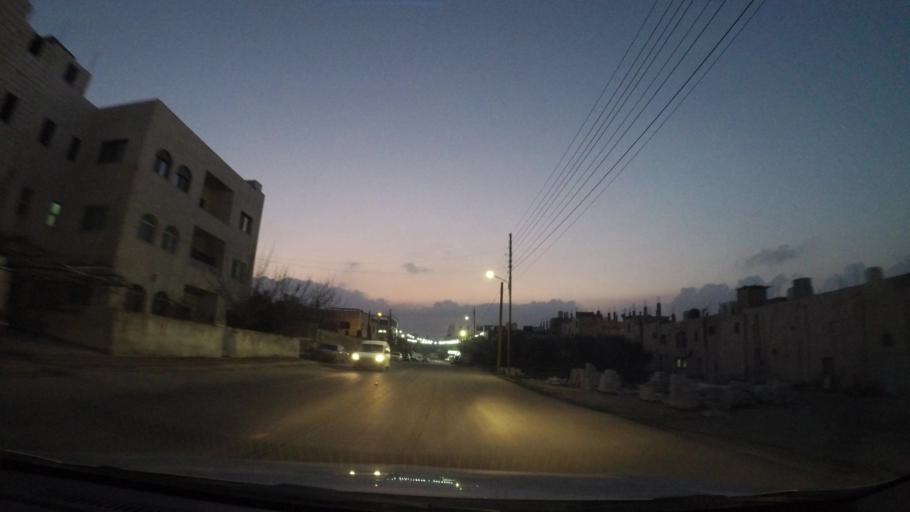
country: JO
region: Amman
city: Al Bunayyat ash Shamaliyah
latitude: 31.8951
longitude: 35.9159
